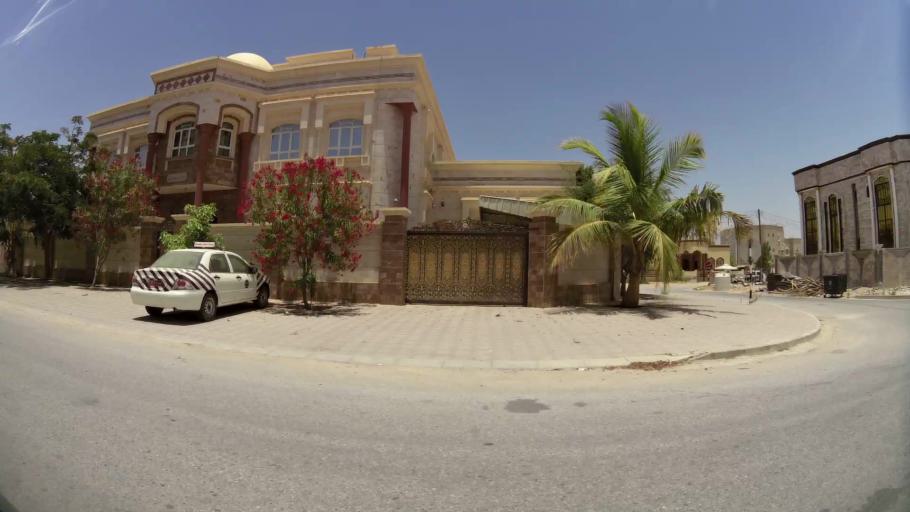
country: OM
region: Zufar
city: Salalah
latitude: 17.0805
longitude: 54.1559
